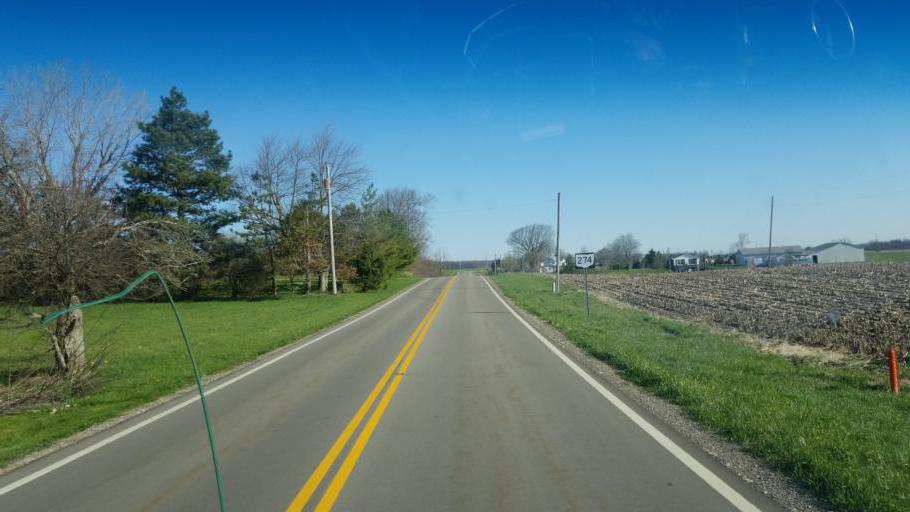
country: US
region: Ohio
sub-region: Logan County
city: Northwood
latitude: 40.5009
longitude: -83.6366
